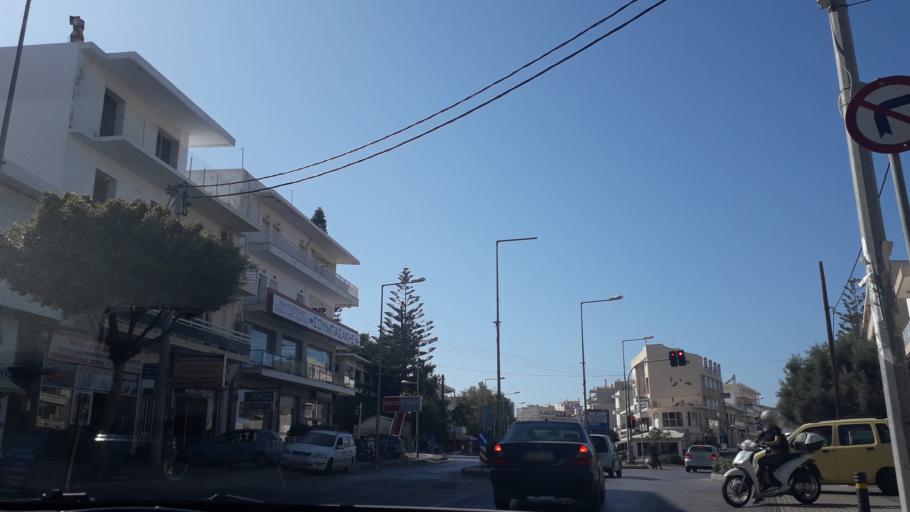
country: GR
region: Crete
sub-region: Nomos Rethymnis
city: Rethymno
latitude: 35.3644
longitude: 24.4853
